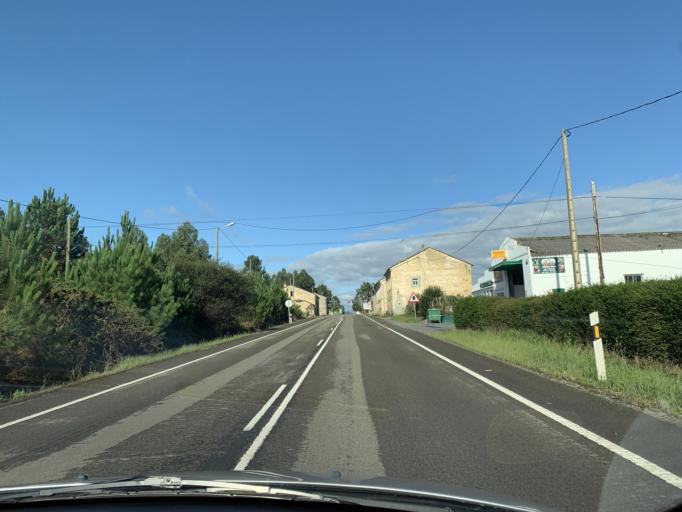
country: ES
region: Galicia
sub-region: Provincia de Lugo
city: Barreiros
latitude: 43.5448
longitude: -7.2132
